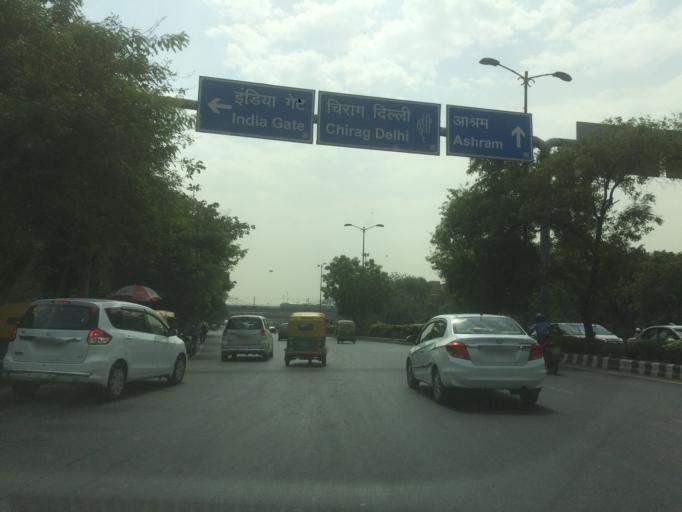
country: IN
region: NCT
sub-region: New Delhi
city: New Delhi
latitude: 28.5659
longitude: 77.2306
